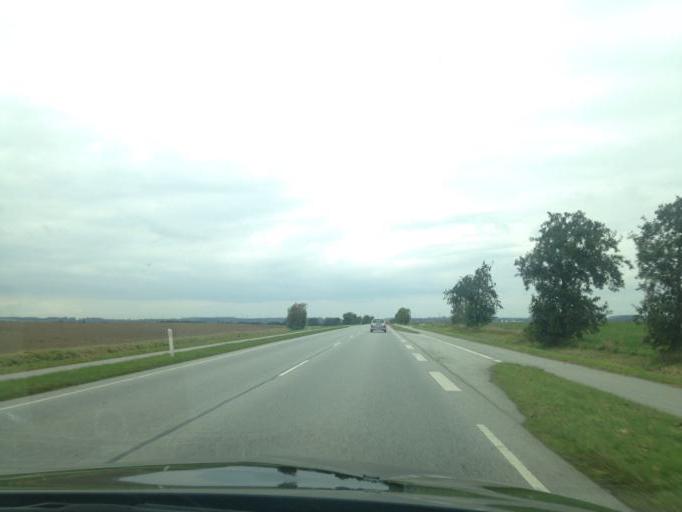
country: DK
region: South Denmark
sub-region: Kolding Kommune
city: Christiansfeld
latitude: 55.3292
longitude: 9.4923
